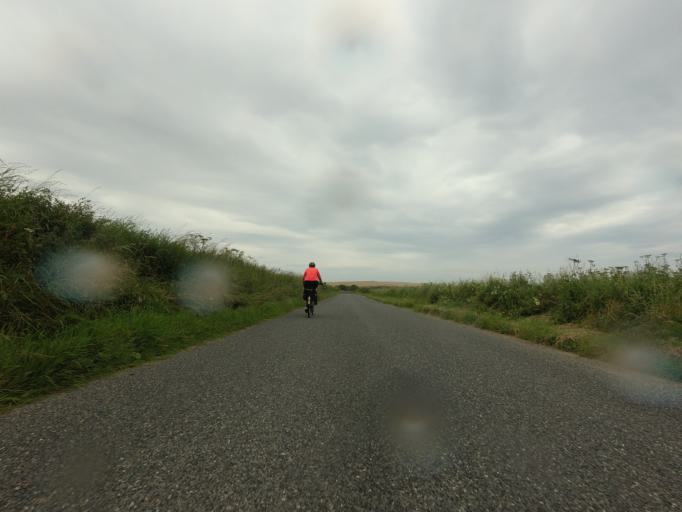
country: GB
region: Scotland
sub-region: Aberdeenshire
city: Portsoy
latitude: 57.6740
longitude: -2.6433
